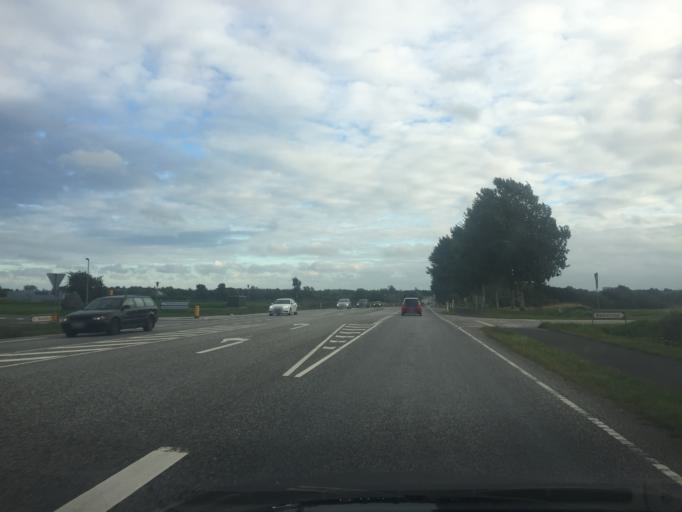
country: DK
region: Zealand
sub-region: Solrod Kommune
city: Havdrup
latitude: 55.5856
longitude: 12.1077
